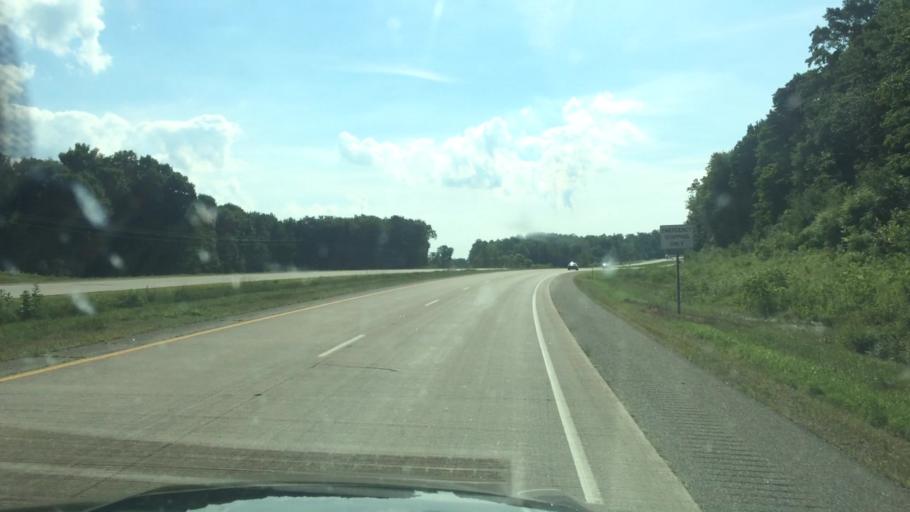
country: US
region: Wisconsin
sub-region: Shawano County
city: Wittenberg
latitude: 44.8259
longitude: -89.0704
